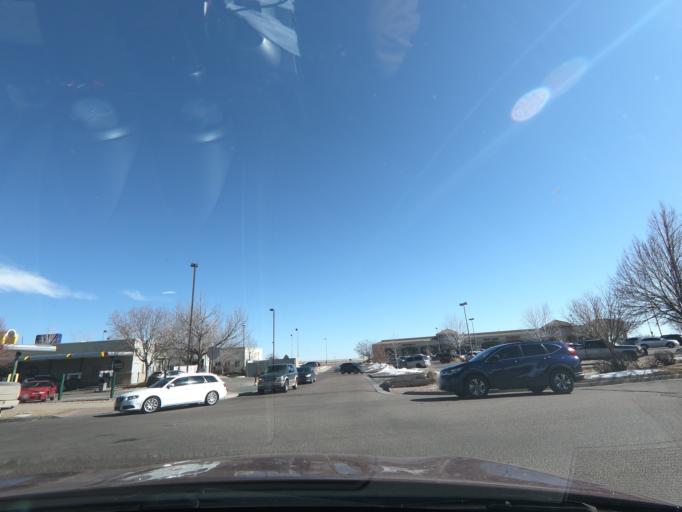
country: US
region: Colorado
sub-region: El Paso County
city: Security-Widefield
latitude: 38.7175
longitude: -104.6981
